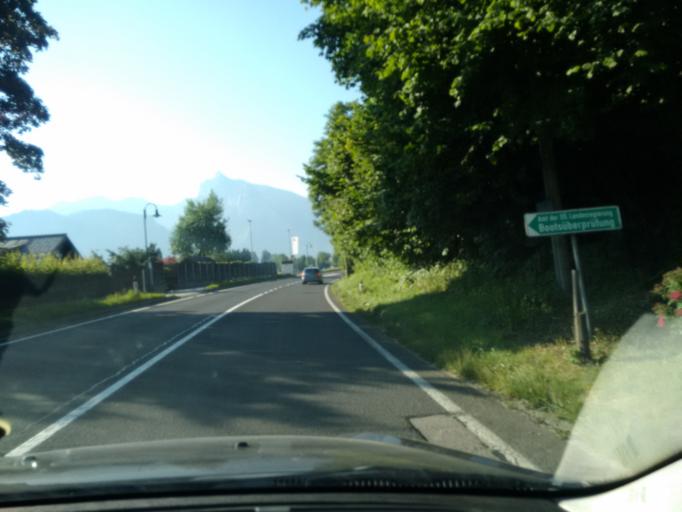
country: AT
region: Upper Austria
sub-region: Politischer Bezirk Gmunden
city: Altmunster
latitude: 47.8602
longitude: 13.7809
